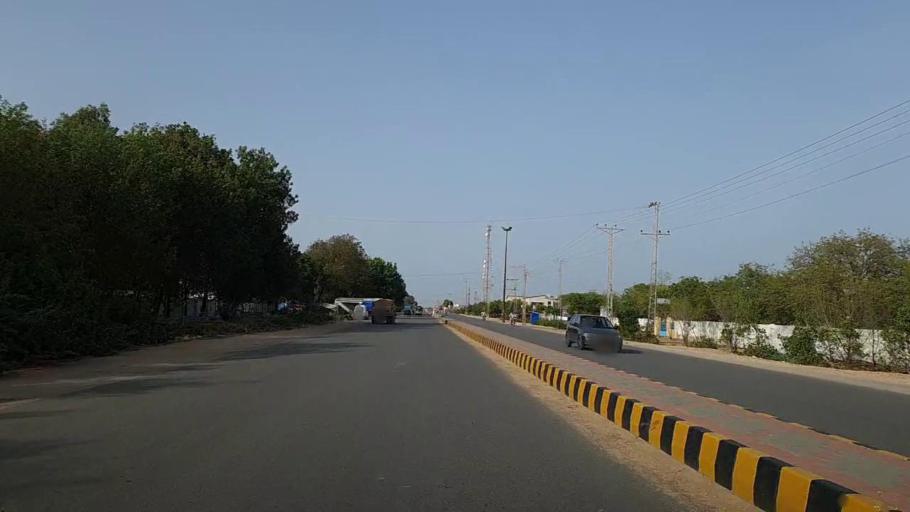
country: PK
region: Sindh
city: Thatta
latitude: 24.7473
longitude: 67.8949
